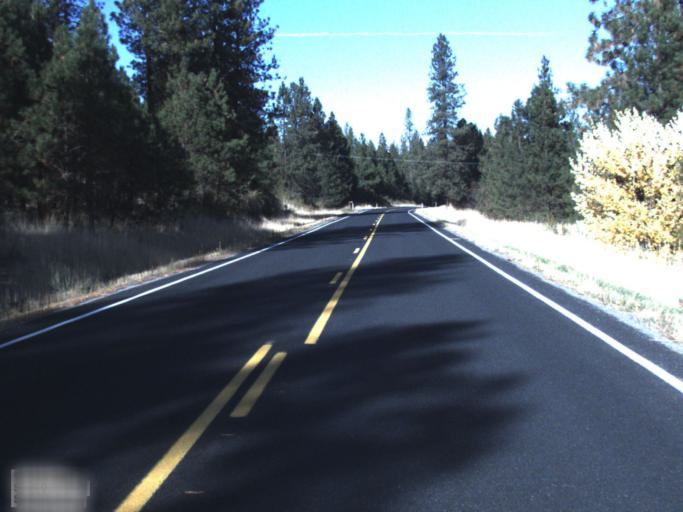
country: US
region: Washington
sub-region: Lincoln County
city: Davenport
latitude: 48.0215
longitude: -118.2361
